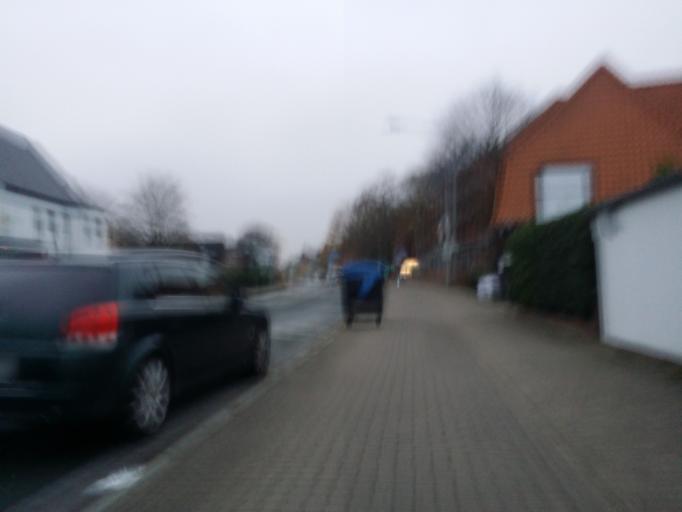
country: DE
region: Lower Saxony
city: Stuhr
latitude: 53.0163
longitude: 8.7893
